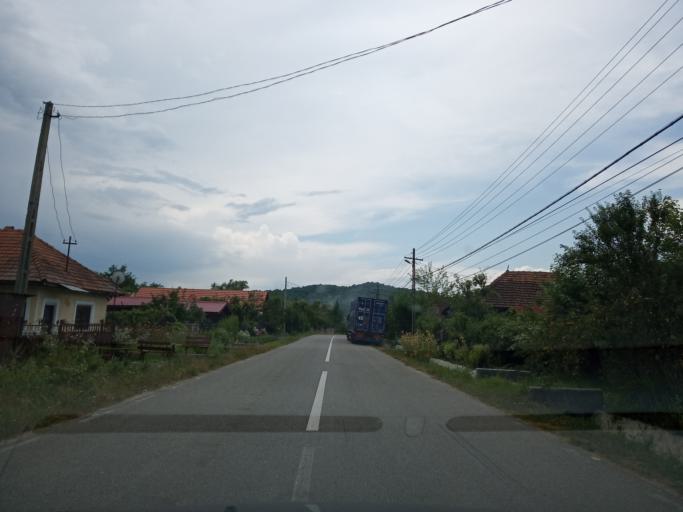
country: RO
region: Gorj
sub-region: Comuna Godinesti
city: Godinesti
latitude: 44.9787
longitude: 22.9525
